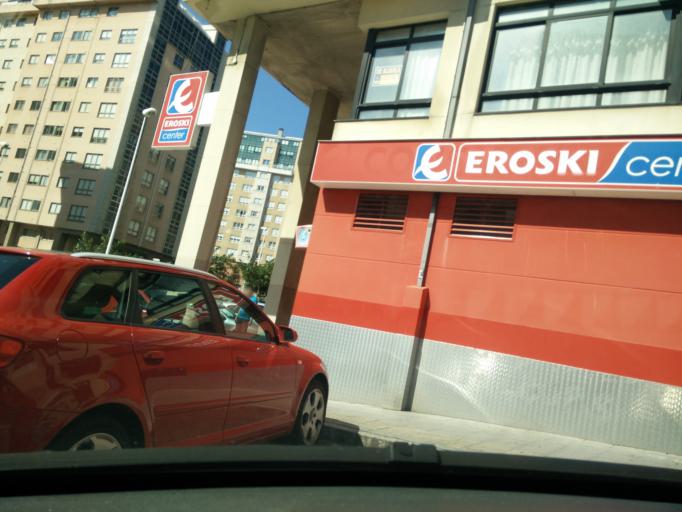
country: ES
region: Galicia
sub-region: Provincia da Coruna
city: A Coruna
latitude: 43.3756
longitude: -8.4325
